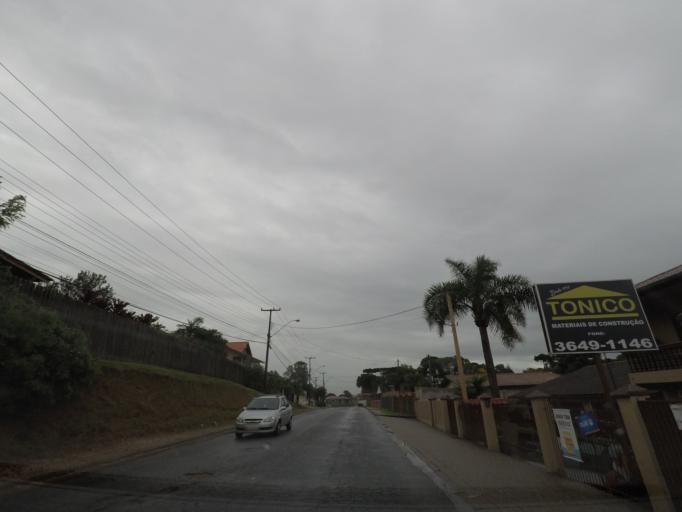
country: BR
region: Parana
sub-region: Curitiba
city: Curitiba
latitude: -25.4625
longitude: -49.3950
